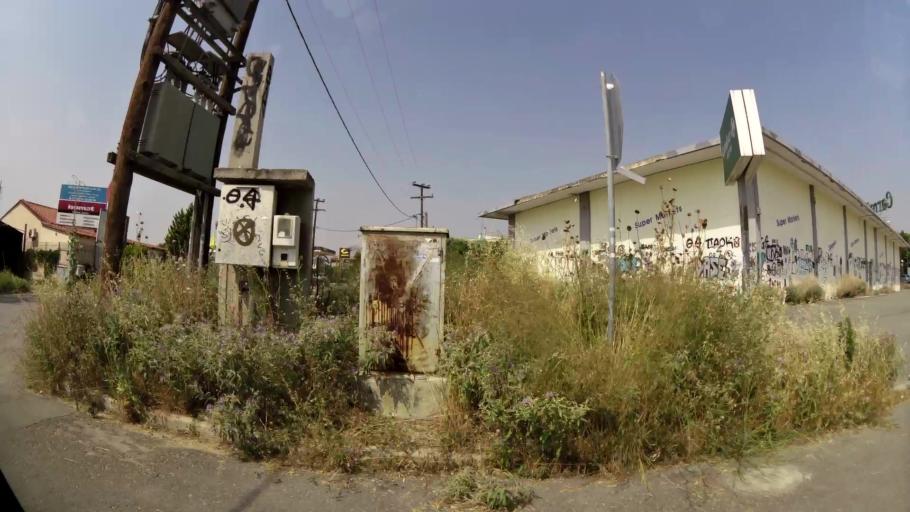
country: GR
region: Central Macedonia
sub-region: Nomos Thessalonikis
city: Efkarpia
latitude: 40.6882
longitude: 22.9483
